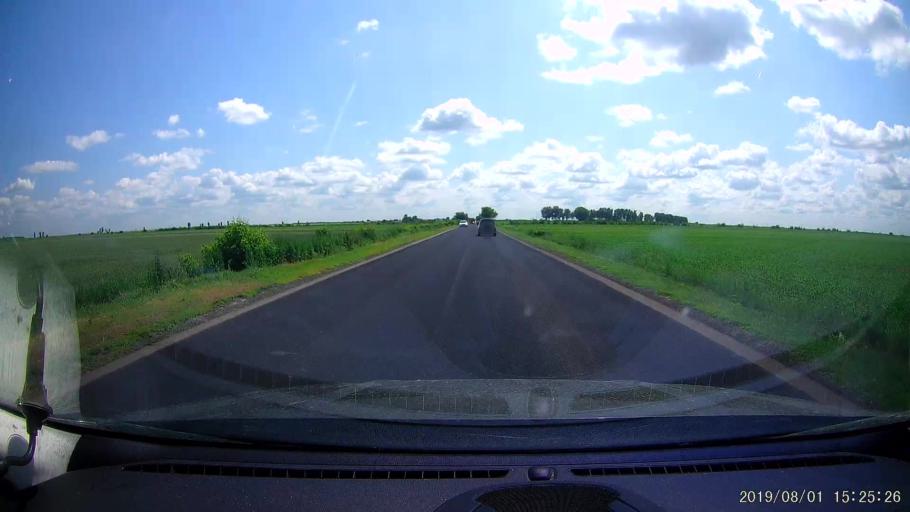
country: RO
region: Braila
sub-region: Comuna Viziru
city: Lanurile
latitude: 45.0220
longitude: 27.7354
